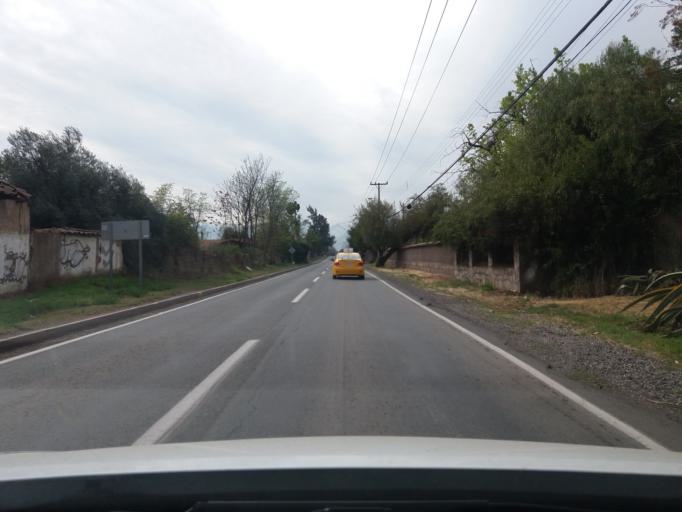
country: CL
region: Valparaiso
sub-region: Provincia de San Felipe
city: San Felipe
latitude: -32.8181
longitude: -70.6857
